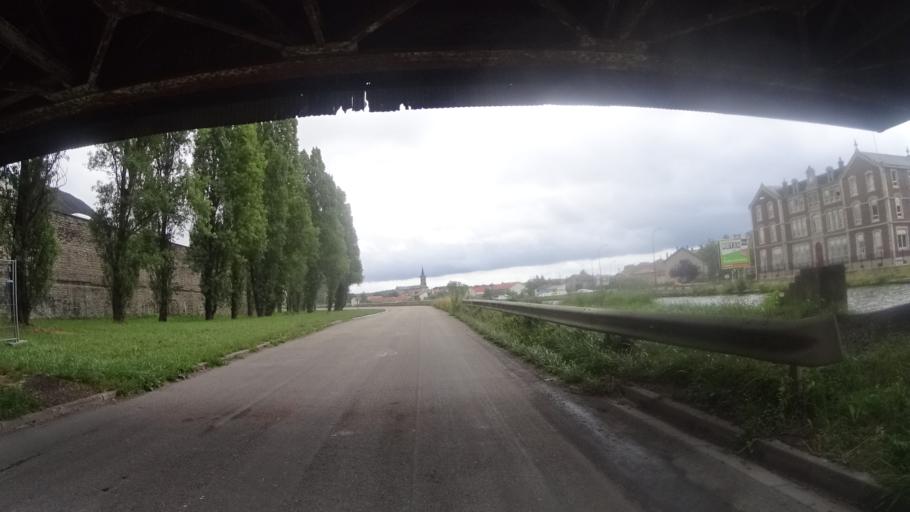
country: FR
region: Lorraine
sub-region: Departement de Meurthe-et-Moselle
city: Dombasle-sur-Meurthe
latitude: 48.6288
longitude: 6.3414
